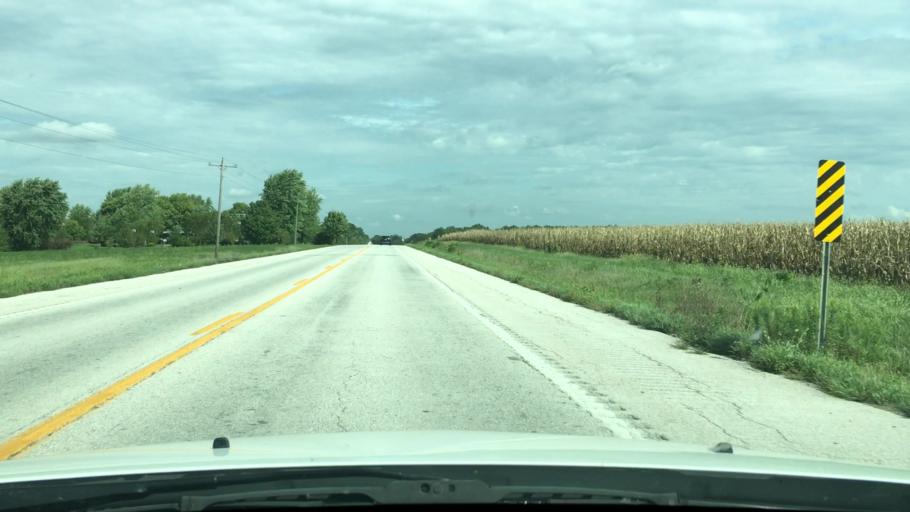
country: US
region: Missouri
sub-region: Montgomery County
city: Wellsville
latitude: 39.1931
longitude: -91.6468
